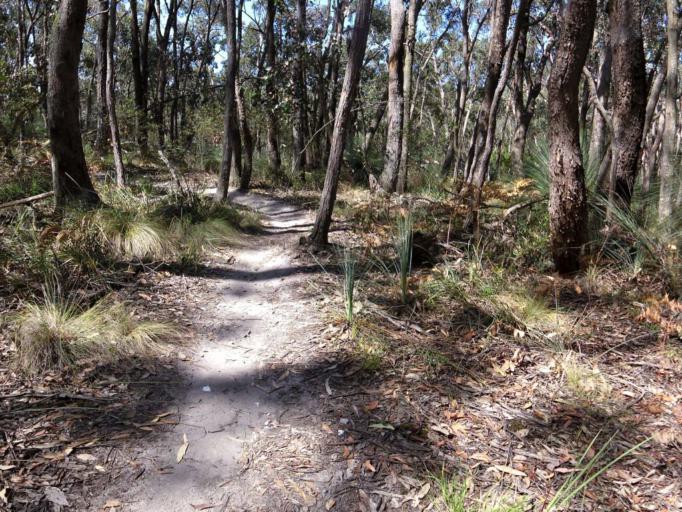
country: AU
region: Victoria
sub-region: Melton
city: Melton West
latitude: -37.5134
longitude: 144.5555
